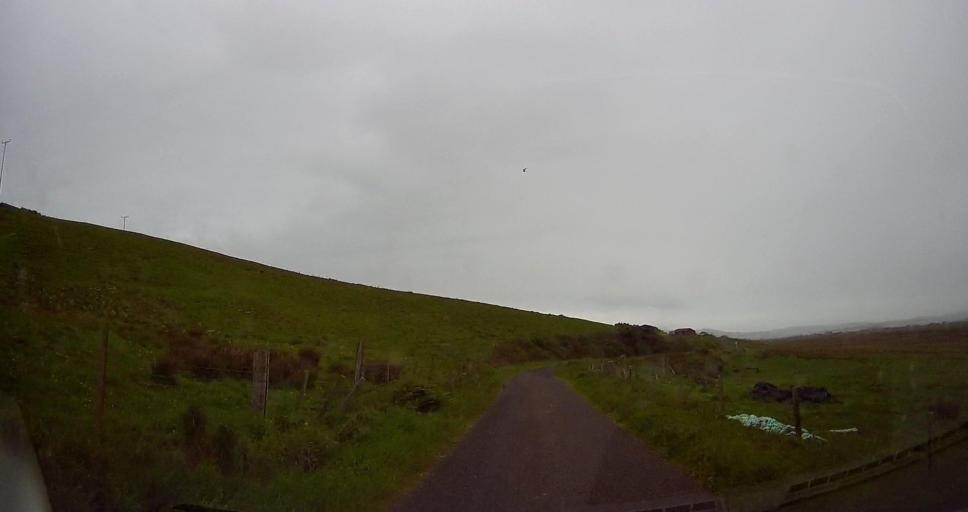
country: GB
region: Scotland
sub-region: Orkney Islands
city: Stromness
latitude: 58.9766
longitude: -3.1627
